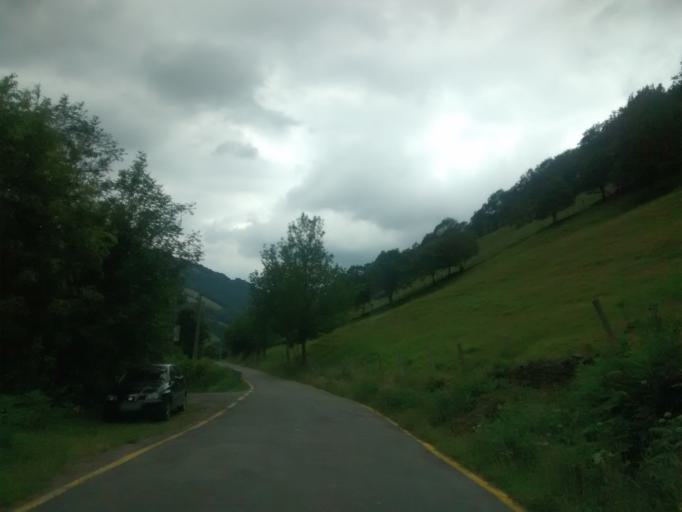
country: ES
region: Cantabria
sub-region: Provincia de Cantabria
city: Vega de Pas
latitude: 43.1393
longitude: -3.7599
